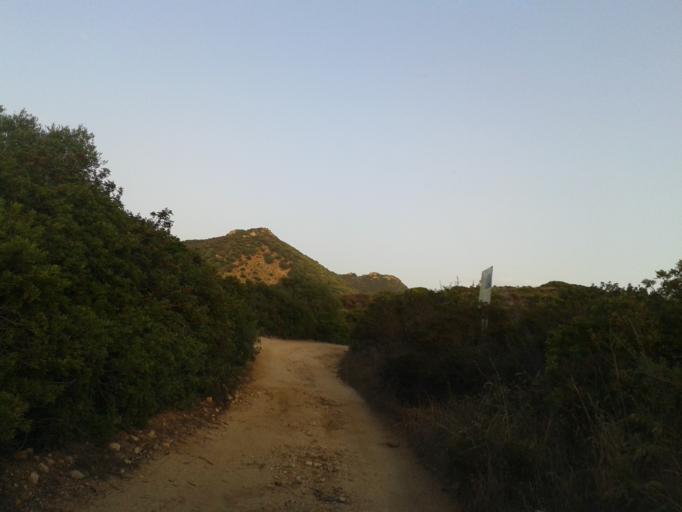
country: IT
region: Sardinia
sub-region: Provincia di Cagliari
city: Villasimius
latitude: 39.1383
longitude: 9.4978
